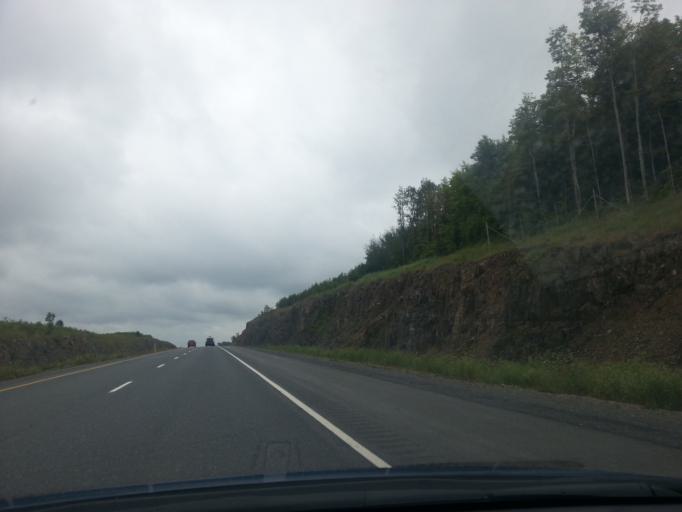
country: CA
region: New Brunswick
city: Florenceville-Bristol
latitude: 46.5016
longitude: -67.6891
